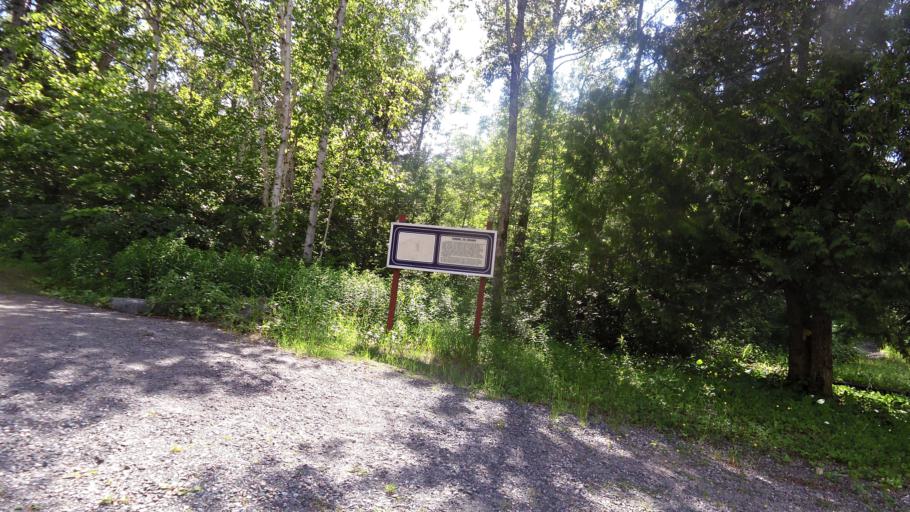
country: CA
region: Ontario
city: Temiskaming Shores
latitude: 47.3860
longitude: -79.6873
